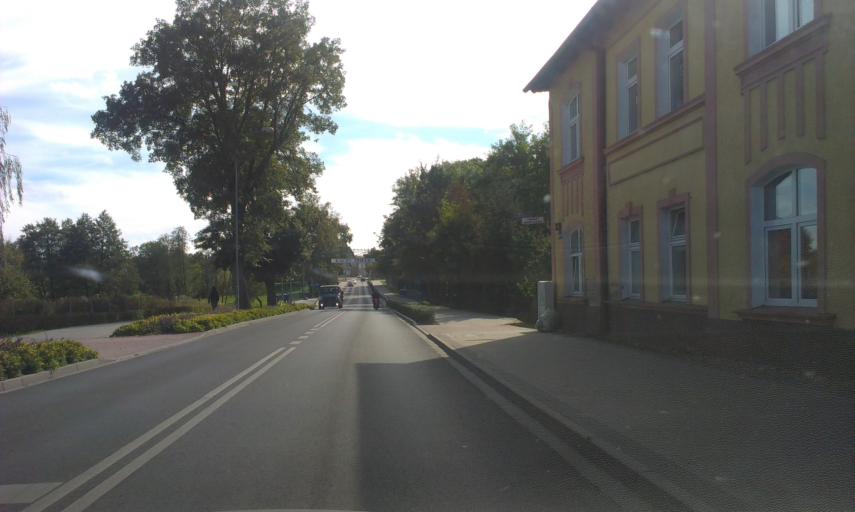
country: PL
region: Greater Poland Voivodeship
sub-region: Powiat zlotowski
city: Zlotow
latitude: 53.3657
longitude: 17.0306
